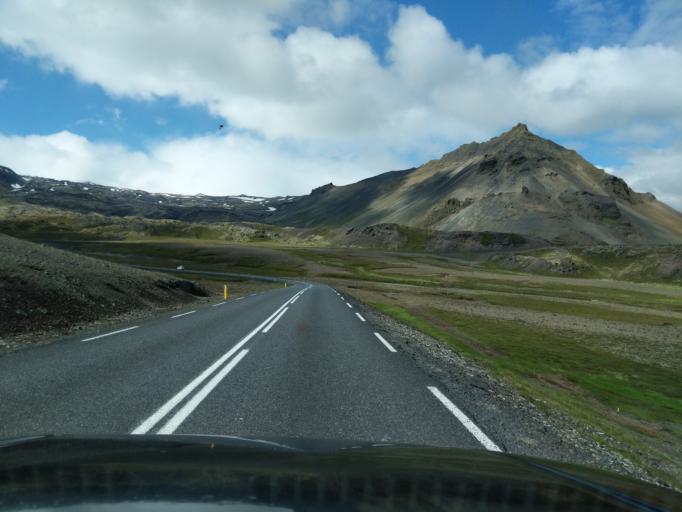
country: IS
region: West
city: Olafsvik
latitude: 64.7574
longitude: -23.6707
